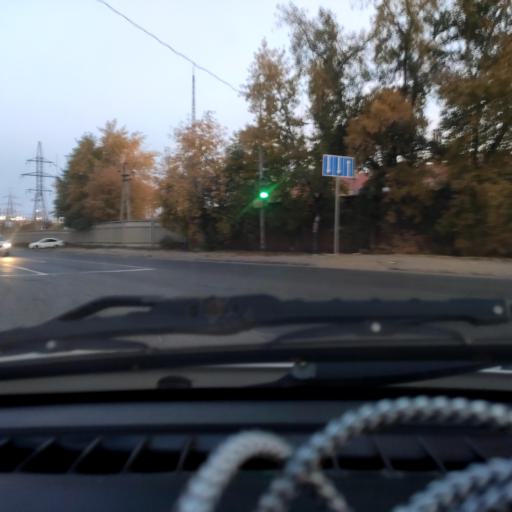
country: RU
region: Samara
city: Zhigulevsk
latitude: 53.4775
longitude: 49.5226
